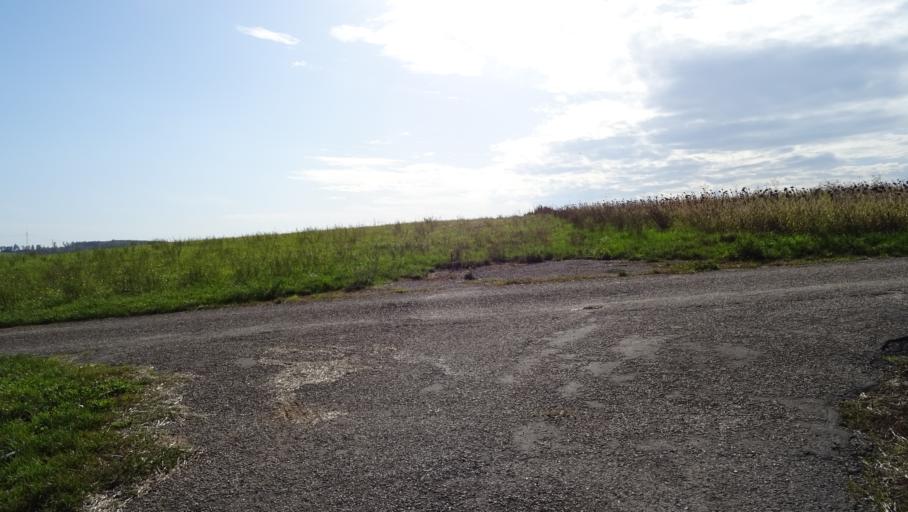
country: DE
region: Baden-Wuerttemberg
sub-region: Karlsruhe Region
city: Billigheim
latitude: 49.3625
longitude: 9.2746
